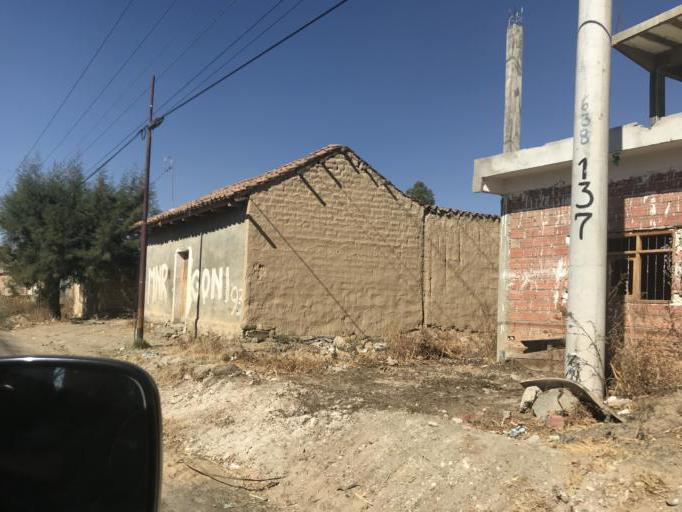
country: BO
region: Cochabamba
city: Punata
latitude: -17.5590
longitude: -65.8681
